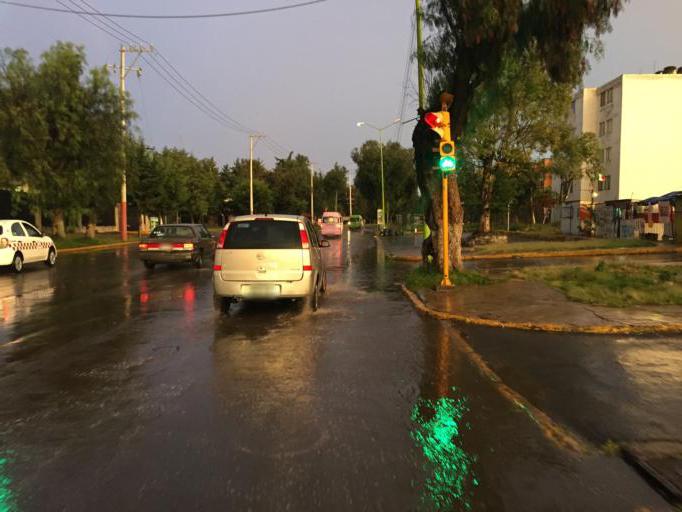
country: MX
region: Mexico
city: Cuautitlan Izcalli
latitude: 19.6741
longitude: -99.2101
